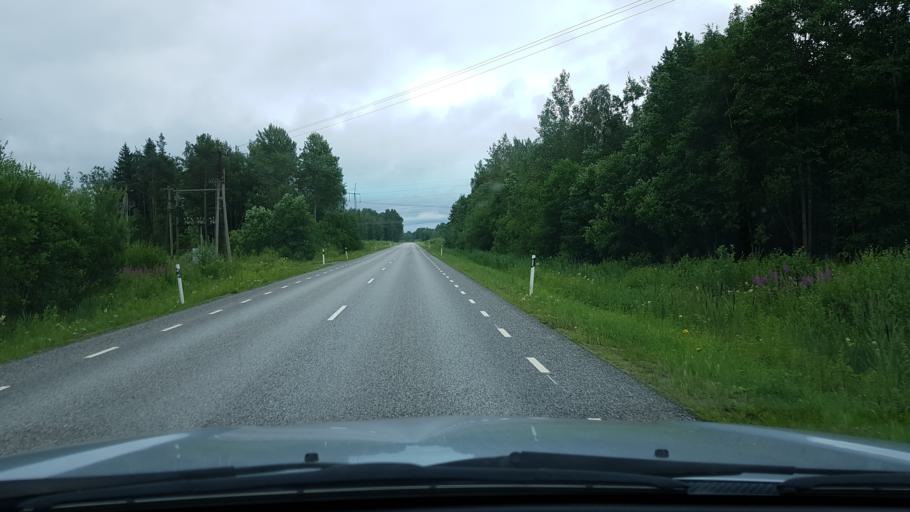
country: EE
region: Ida-Virumaa
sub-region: Narva-Joesuu linn
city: Narva-Joesuu
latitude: 59.3530
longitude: 27.9287
